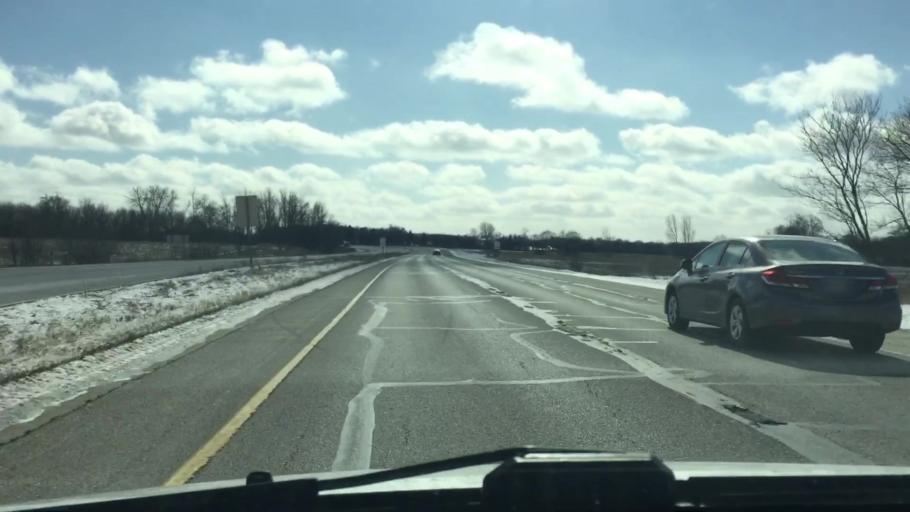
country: US
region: Wisconsin
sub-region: Waukesha County
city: Big Bend
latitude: 42.9294
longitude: -88.2288
